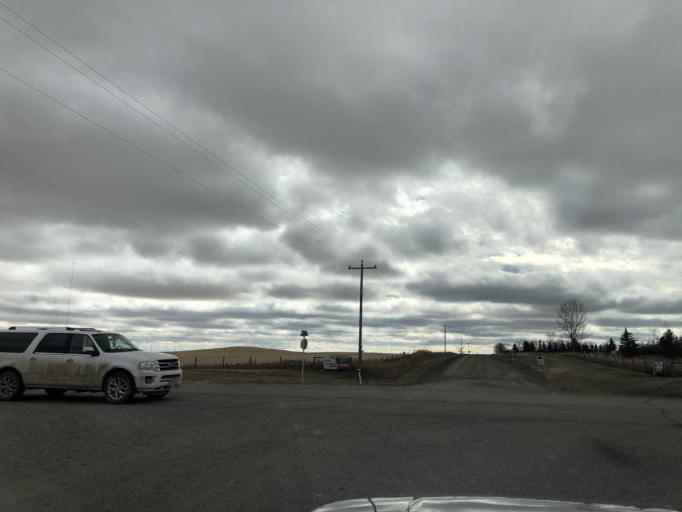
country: CA
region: Alberta
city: Chestermere
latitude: 50.9073
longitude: -113.8830
